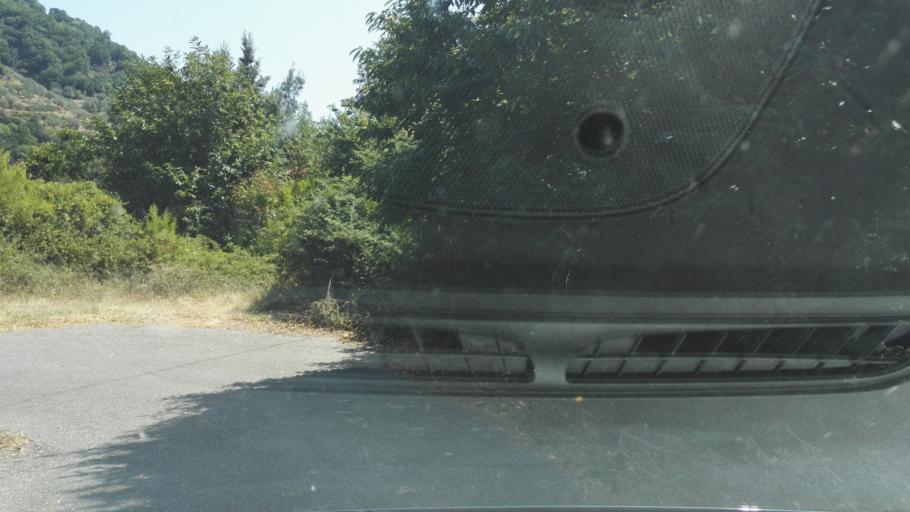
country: IT
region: Calabria
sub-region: Provincia di Reggio Calabria
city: Bivongi
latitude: 38.4903
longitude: 16.4195
